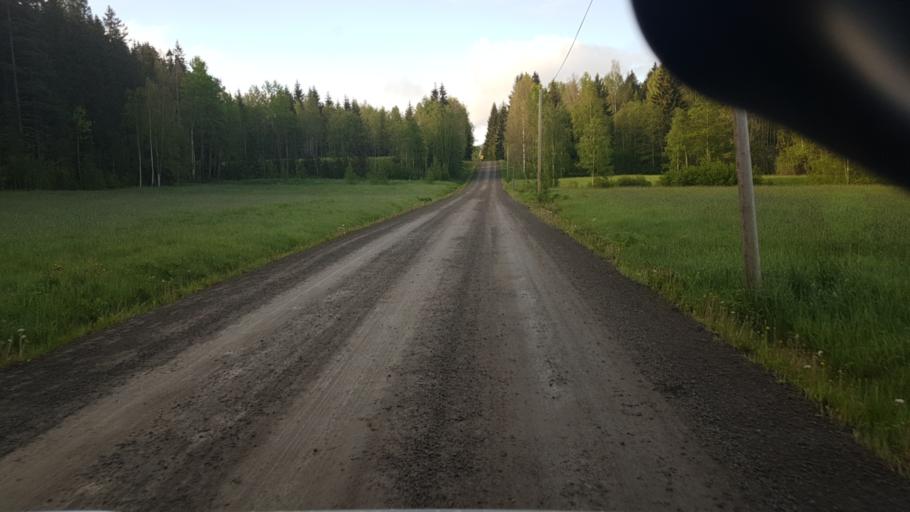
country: SE
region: Vaermland
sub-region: Eda Kommun
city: Amotfors
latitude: 59.7763
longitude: 12.3419
